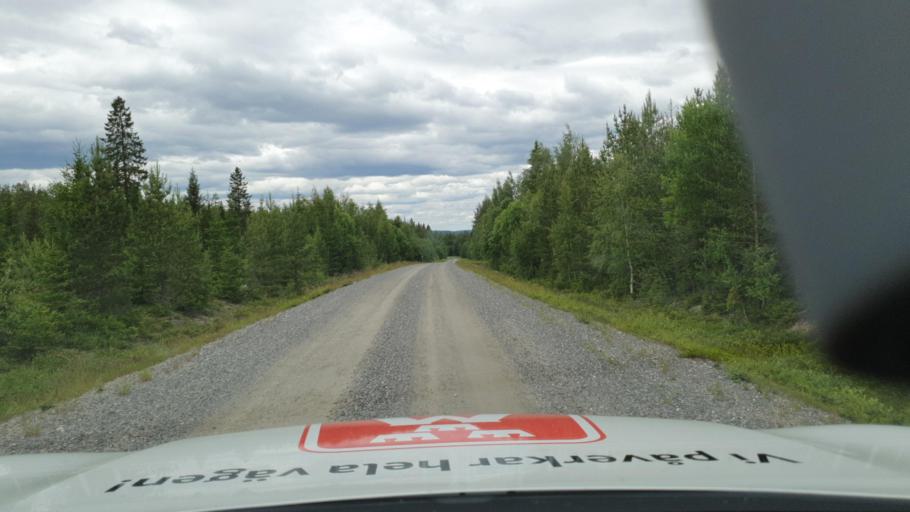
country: SE
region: Vaesterbotten
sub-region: Nordmalings Kommun
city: Nordmaling
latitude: 63.7487
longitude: 19.3767
